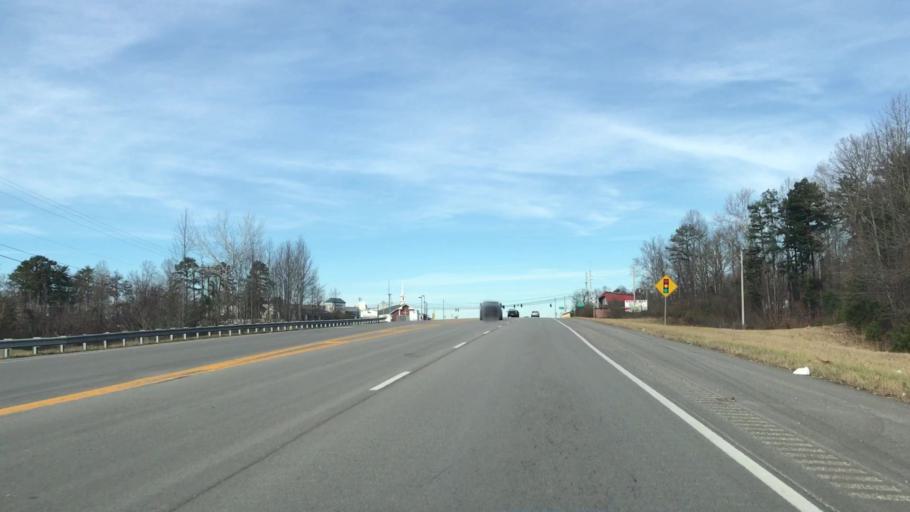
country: US
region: Kentucky
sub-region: McCreary County
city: Whitley City
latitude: 36.7202
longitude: -84.4661
